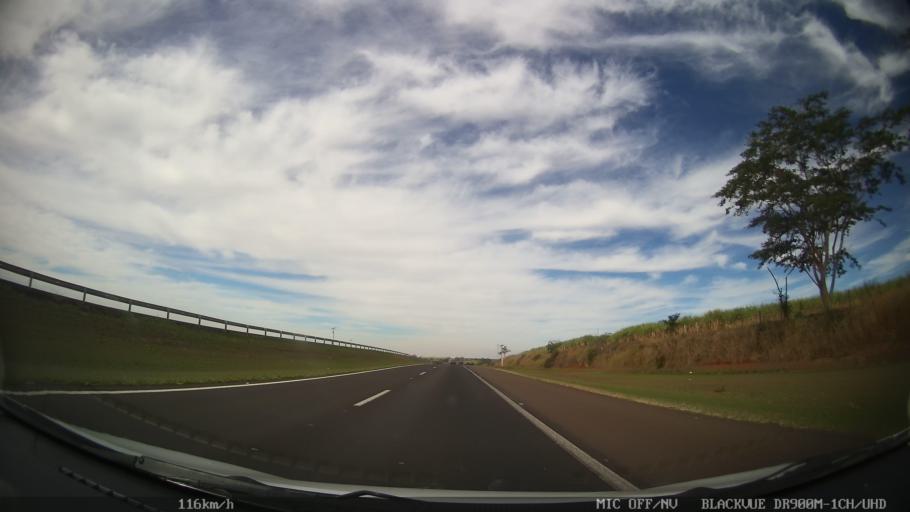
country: BR
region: Sao Paulo
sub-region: Taquaritinga
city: Taquaritinga
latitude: -21.5124
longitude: -48.5454
